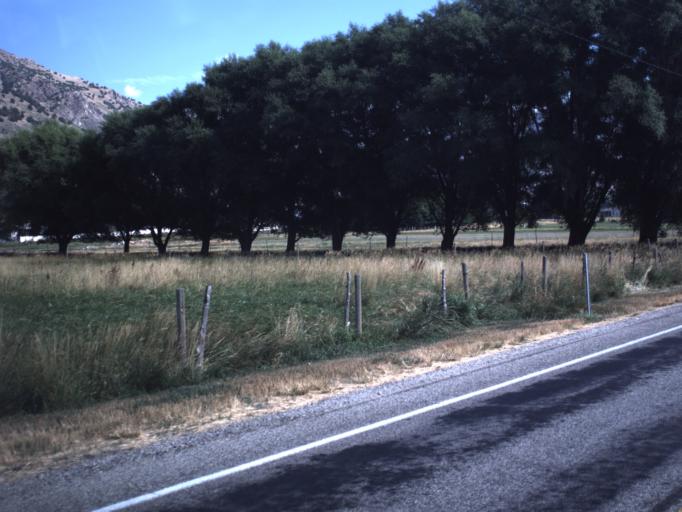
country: US
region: Utah
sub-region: Box Elder County
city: Brigham City
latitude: 41.5391
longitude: -112.0153
